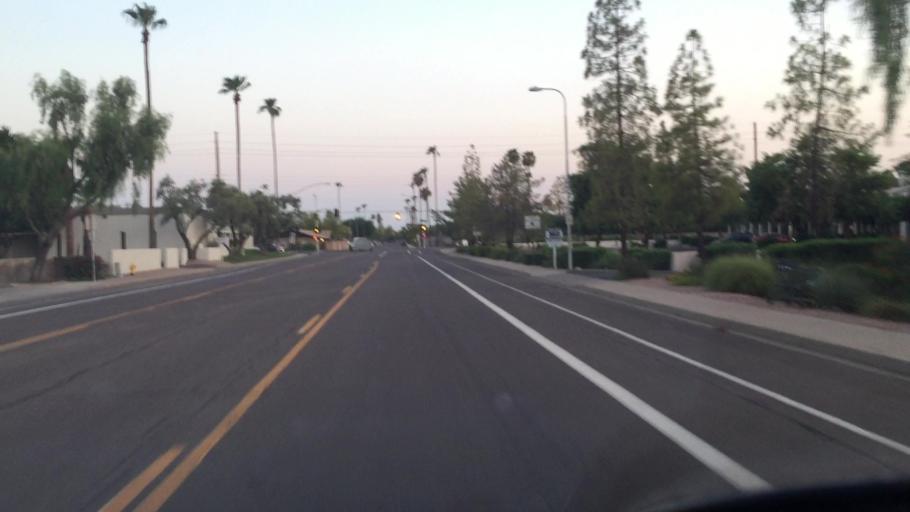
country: US
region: Arizona
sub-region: Maricopa County
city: Tempe
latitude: 33.3943
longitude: -111.9006
